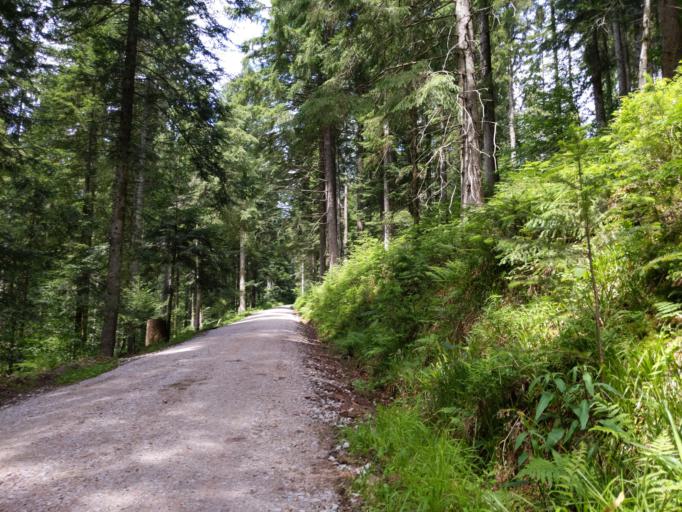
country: DE
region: Baden-Wuerttemberg
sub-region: Karlsruhe Region
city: Freudenstadt
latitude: 48.4398
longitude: 8.3710
